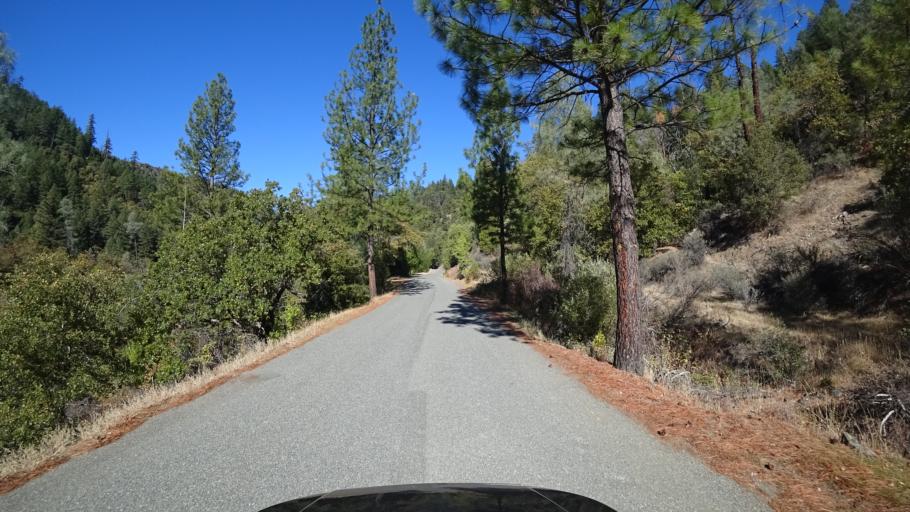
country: US
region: California
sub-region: Humboldt County
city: Willow Creek
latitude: 41.2233
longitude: -123.2501
